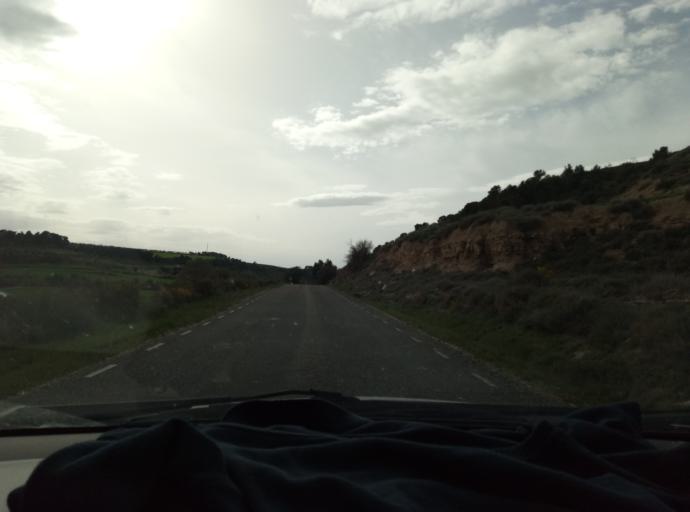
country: ES
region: Catalonia
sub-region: Provincia de Tarragona
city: Vallfogona de Riucorb
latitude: 41.6033
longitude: 1.2163
